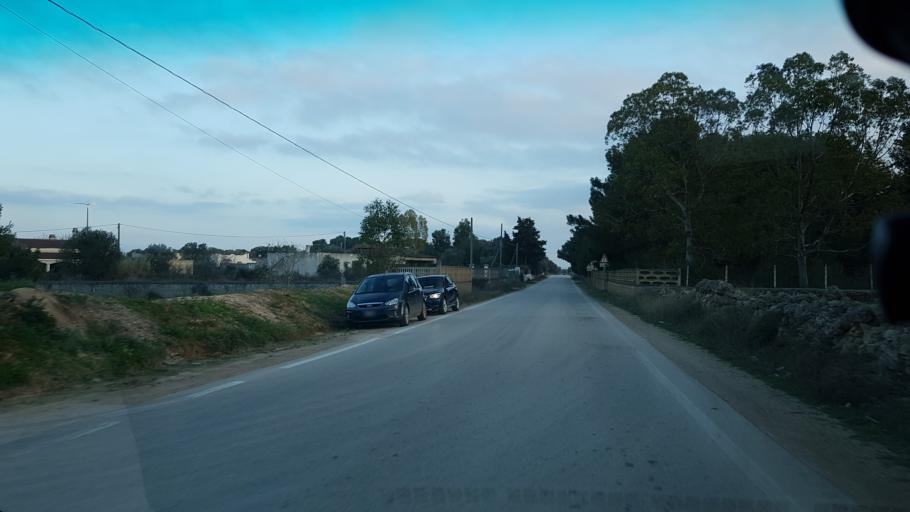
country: IT
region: Apulia
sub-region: Provincia di Brindisi
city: San Vito dei Normanni
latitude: 40.6439
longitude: 17.7776
